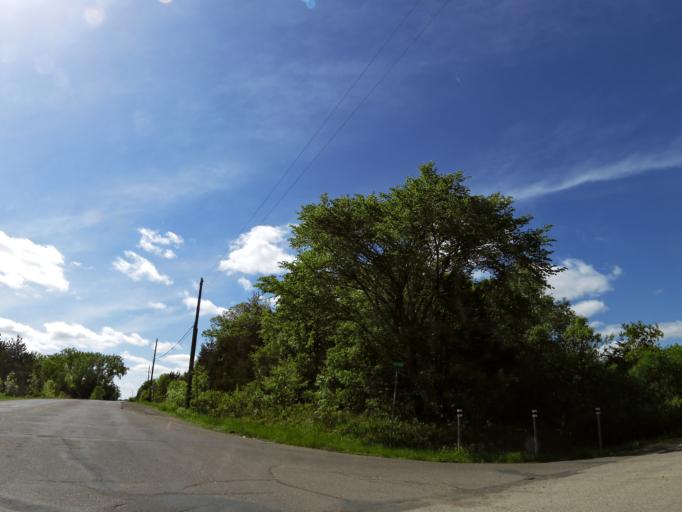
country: US
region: Wisconsin
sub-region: Saint Croix County
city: Hudson
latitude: 44.9799
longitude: -92.7777
